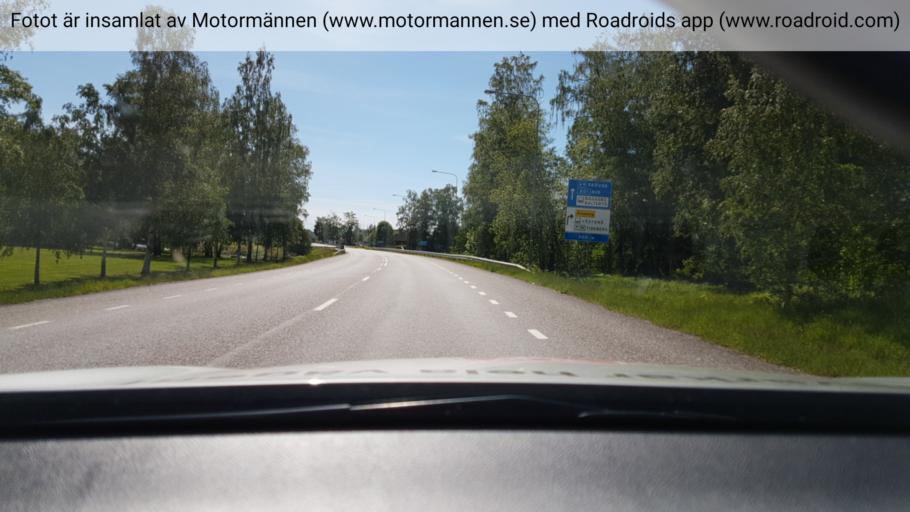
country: SE
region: Vaestra Goetaland
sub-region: Tibro Kommun
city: Tibro
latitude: 58.4284
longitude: 14.1446
